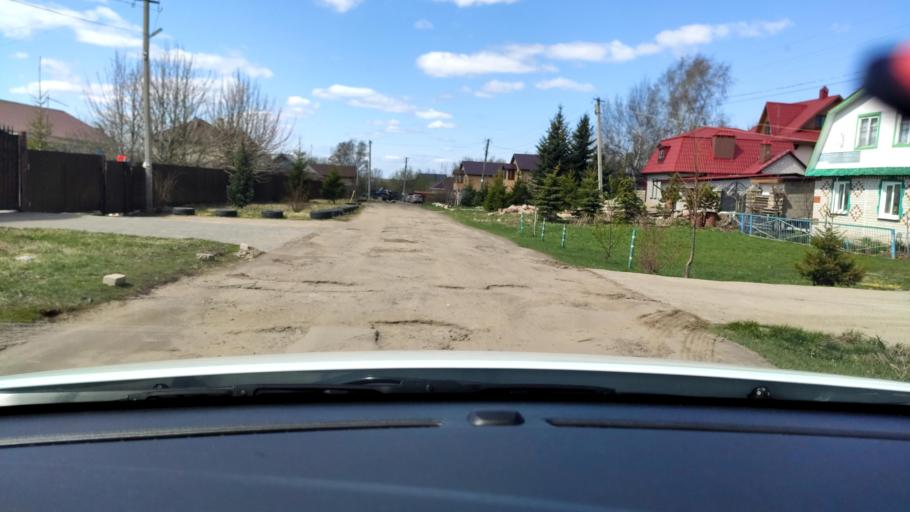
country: RU
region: Tatarstan
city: Stolbishchi
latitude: 55.7178
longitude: 49.3522
